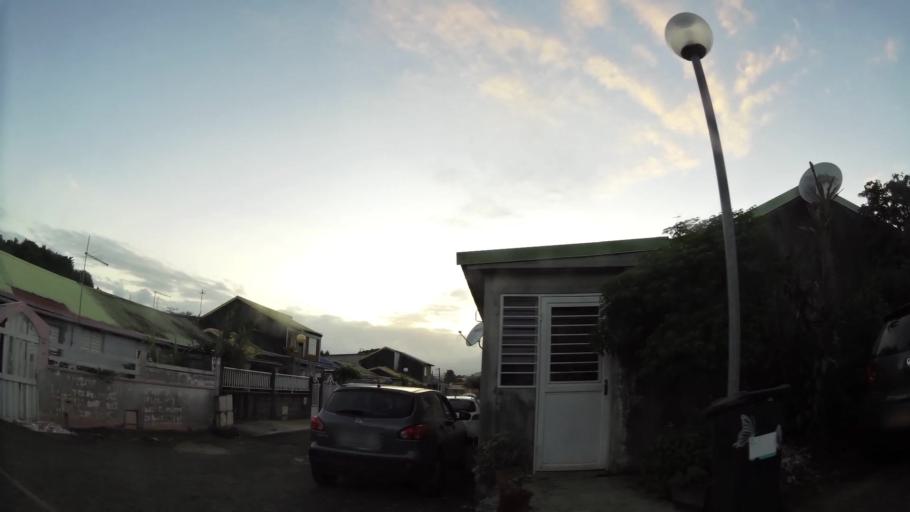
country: GP
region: Guadeloupe
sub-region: Guadeloupe
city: Les Abymes
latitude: 16.2817
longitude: -61.5008
